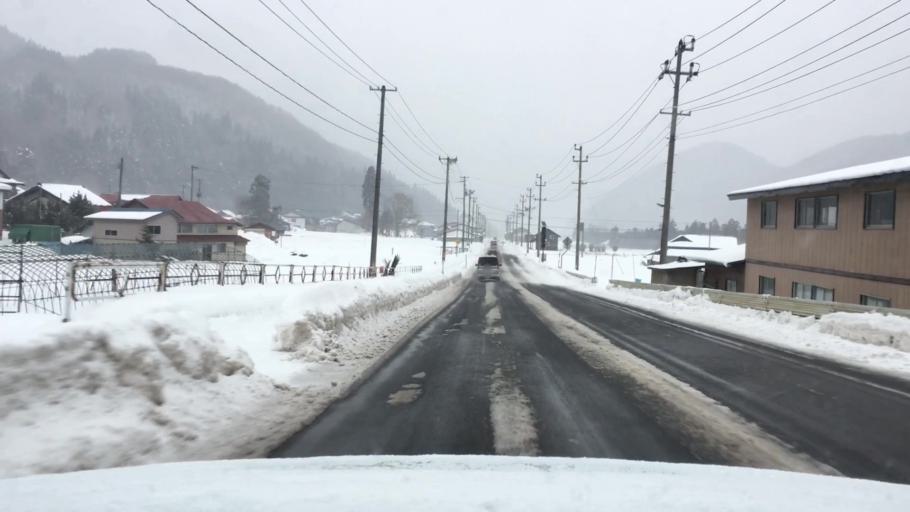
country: JP
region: Akita
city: Hanawa
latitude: 40.0659
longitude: 141.0157
